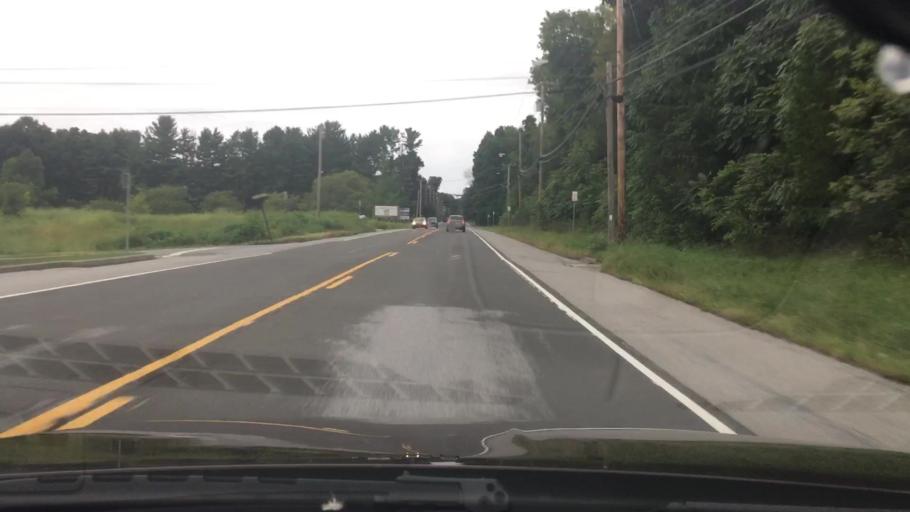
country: US
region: New York
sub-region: Dutchess County
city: Pleasant Valley
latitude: 41.7259
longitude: -73.8422
